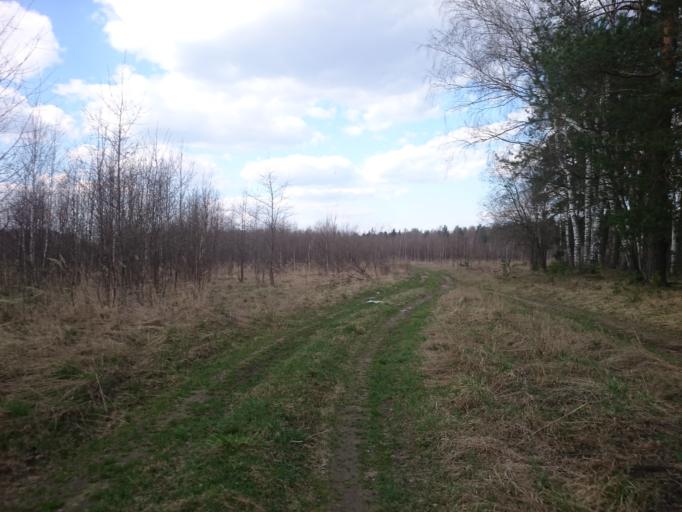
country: RU
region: Moskovskaya
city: Klin
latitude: 56.3995
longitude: 36.6808
